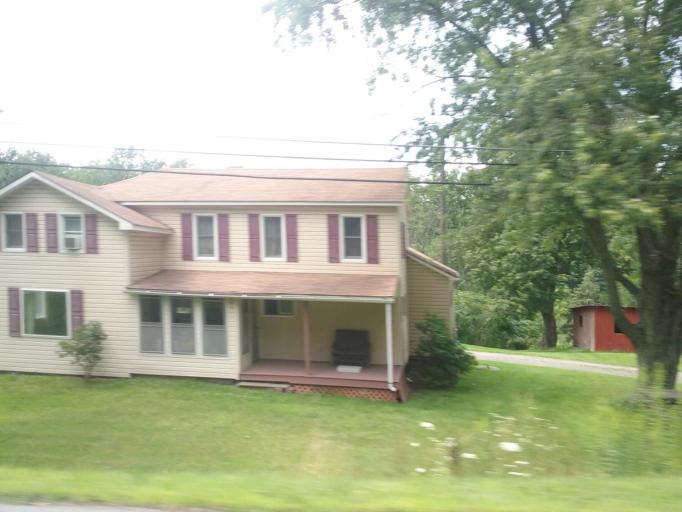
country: US
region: Pennsylvania
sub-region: Tioga County
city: Wellsboro
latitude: 41.7441
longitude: -77.2528
